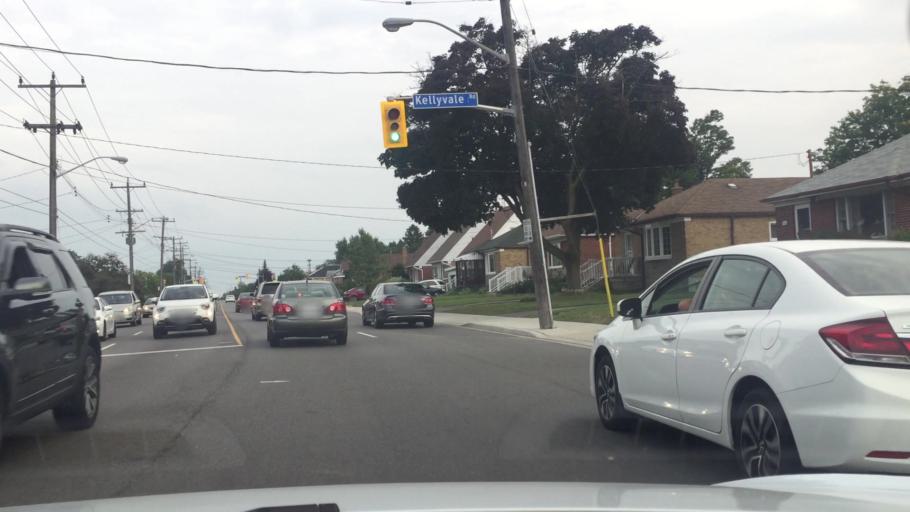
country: CA
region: Ontario
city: Scarborough
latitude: 43.7571
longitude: -79.3102
